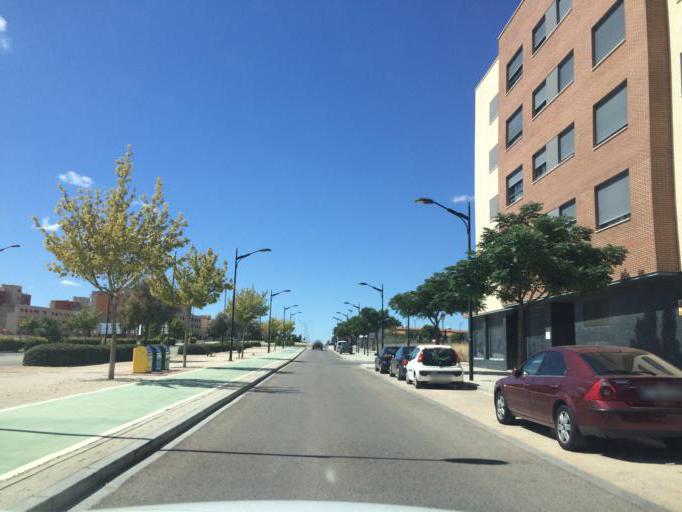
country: ES
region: Castille-La Mancha
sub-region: Provincia de Albacete
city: Albacete
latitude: 38.9774
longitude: -1.8439
